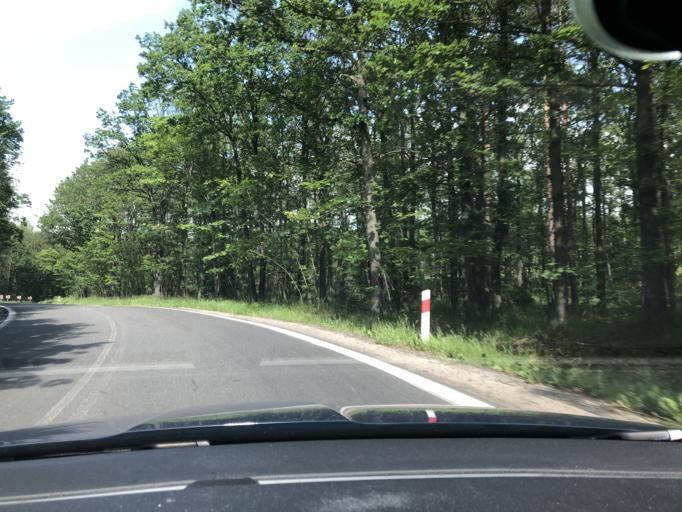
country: PL
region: Lower Silesian Voivodeship
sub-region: Powiat jaworski
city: Bolkow
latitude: 50.9430
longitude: 16.1133
